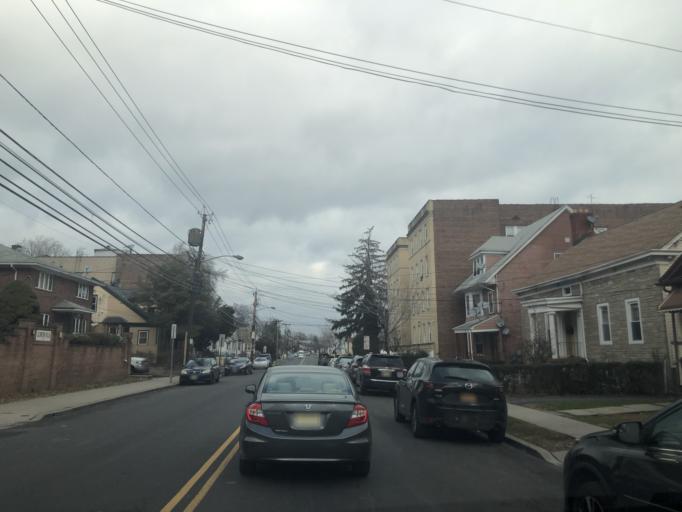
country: US
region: New Jersey
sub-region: Essex County
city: Irvington
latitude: 40.7293
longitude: -74.2360
